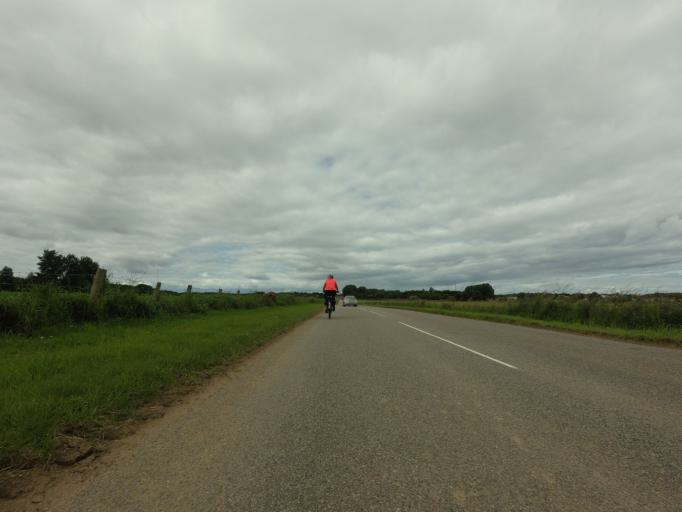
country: GB
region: Scotland
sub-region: Moray
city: Kinloss
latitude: 57.6298
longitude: -3.5522
